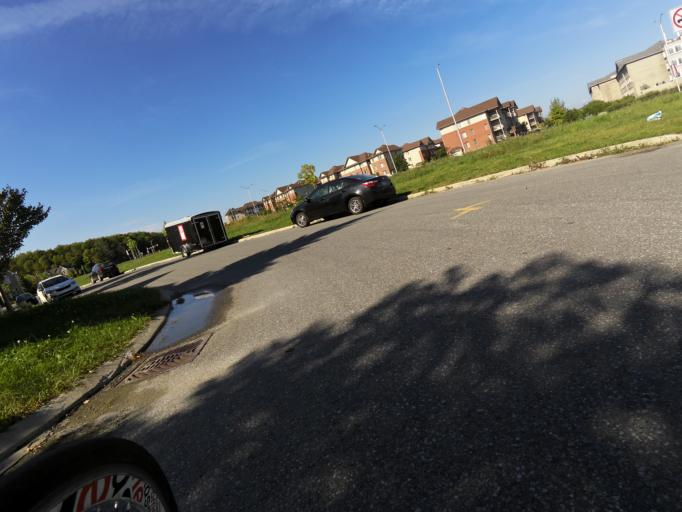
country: CA
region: Ontario
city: Bells Corners
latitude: 45.2706
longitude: -75.7078
